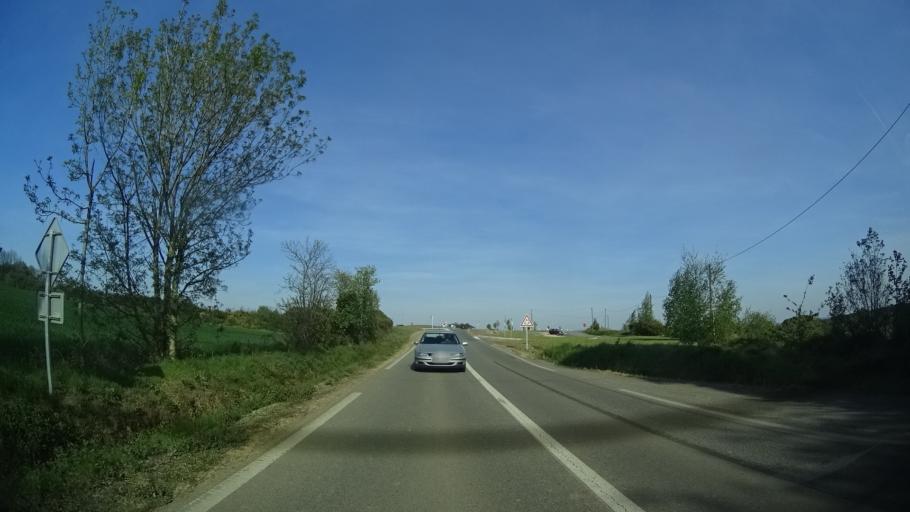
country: FR
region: Brittany
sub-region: Departement du Morbihan
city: Allaire
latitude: 47.6127
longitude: -2.1496
